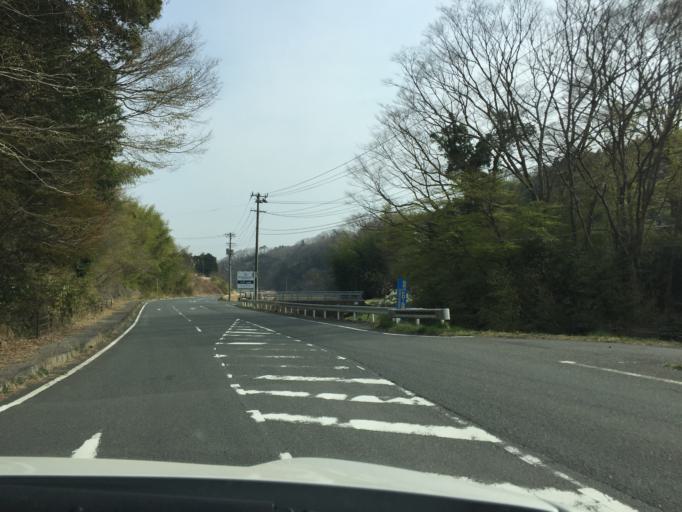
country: JP
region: Fukushima
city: Iwaki
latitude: 36.9970
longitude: 140.7897
